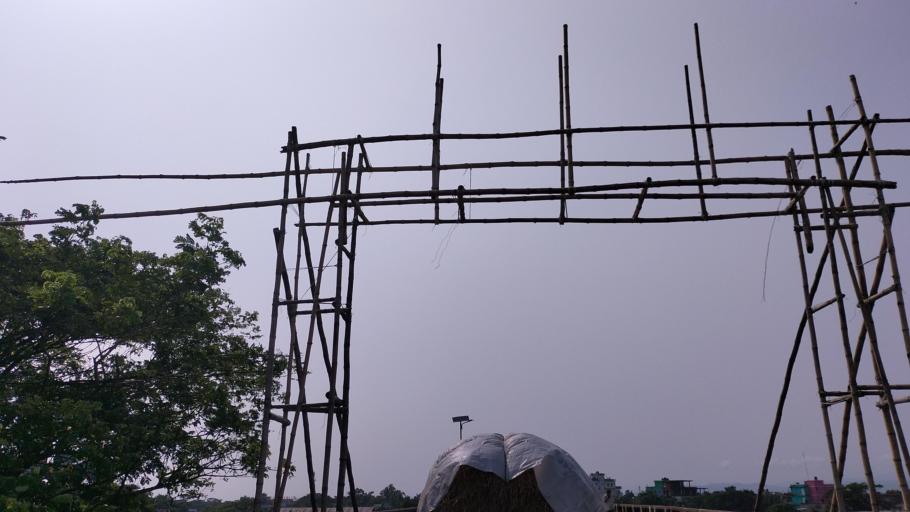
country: BD
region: Dhaka
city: Netrakona
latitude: 25.0742
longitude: 90.8914
